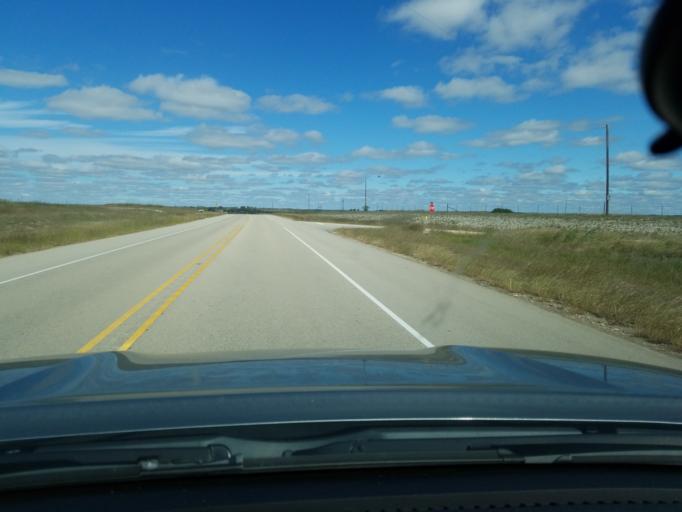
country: US
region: Texas
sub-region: Hamilton County
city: Hamilton
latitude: 31.6291
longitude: -98.1534
